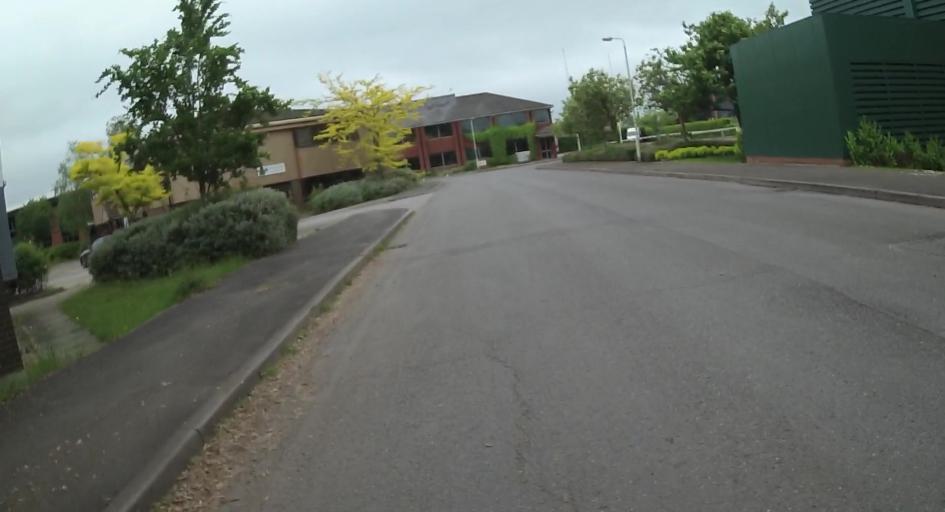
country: GB
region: England
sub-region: Hampshire
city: Eversley
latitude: 51.3743
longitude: -0.8935
